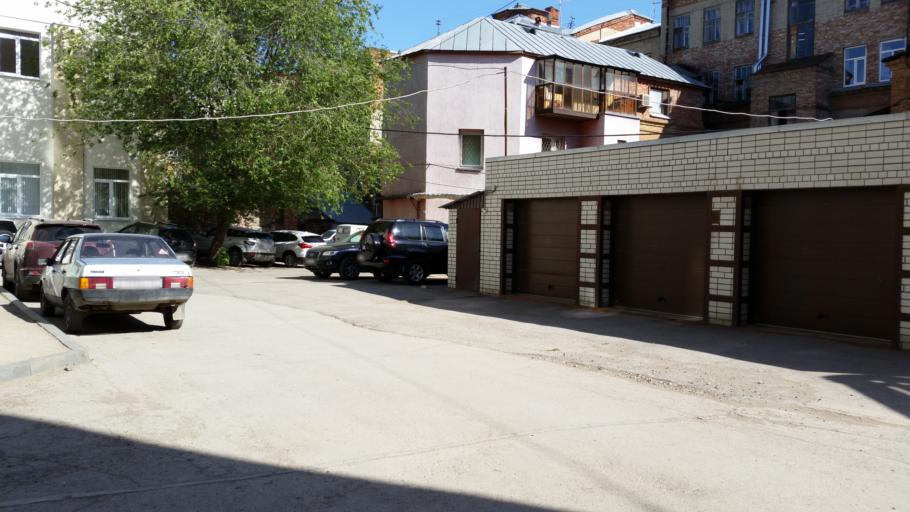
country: RU
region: Saratov
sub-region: Saratovskiy Rayon
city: Saratov
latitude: 51.5331
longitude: 46.0231
